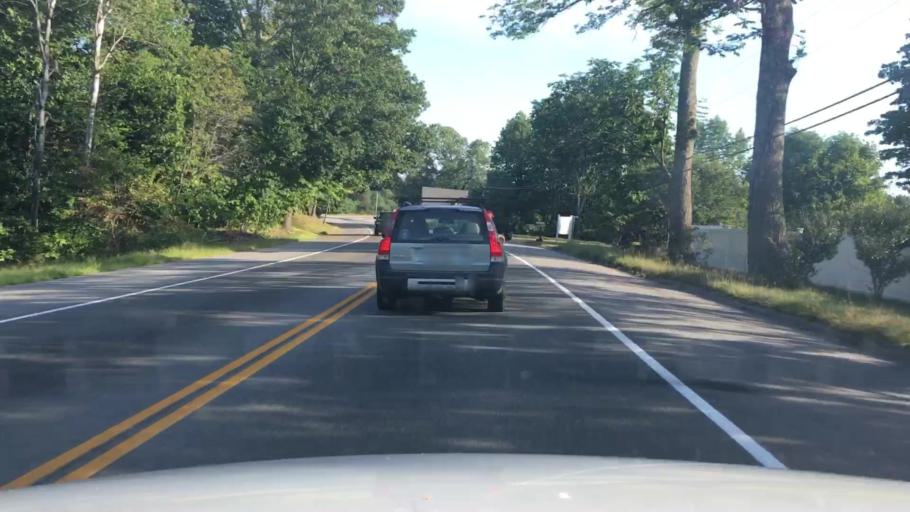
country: US
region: Maine
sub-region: Cumberland County
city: Cumberland Center
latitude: 43.7569
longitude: -70.3013
